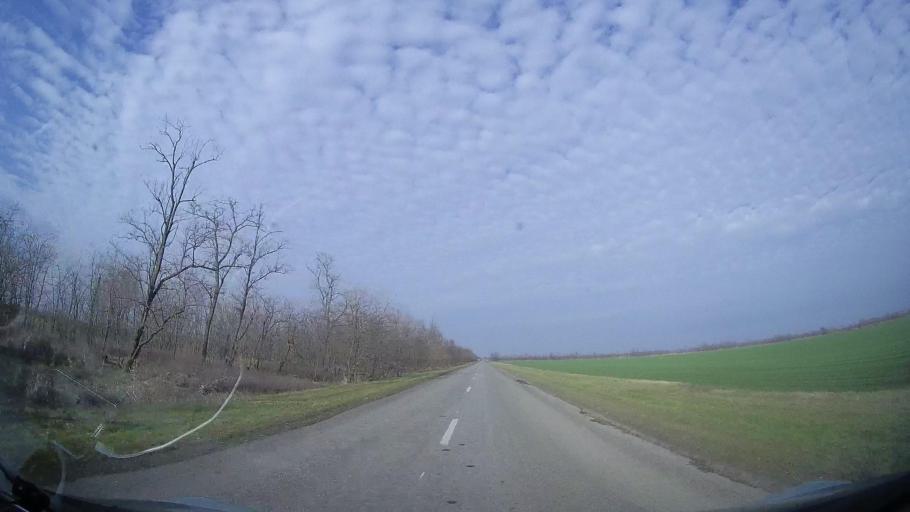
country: RU
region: Rostov
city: Gigant
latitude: 46.8715
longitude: 41.2743
